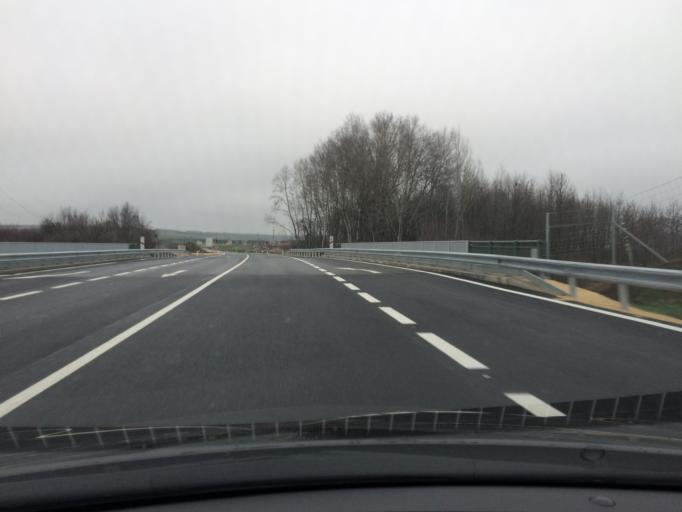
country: AT
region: Lower Austria
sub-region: Politischer Bezirk Mistelbach
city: Mistelbach
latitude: 48.5558
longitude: 16.5584
